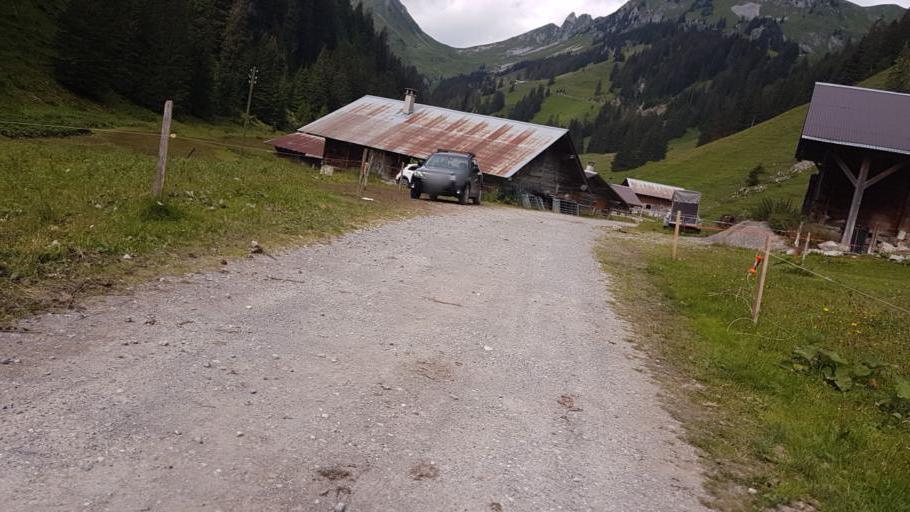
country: CH
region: Bern
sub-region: Obersimmental-Saanen District
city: Boltigen
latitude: 46.6896
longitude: 7.4423
